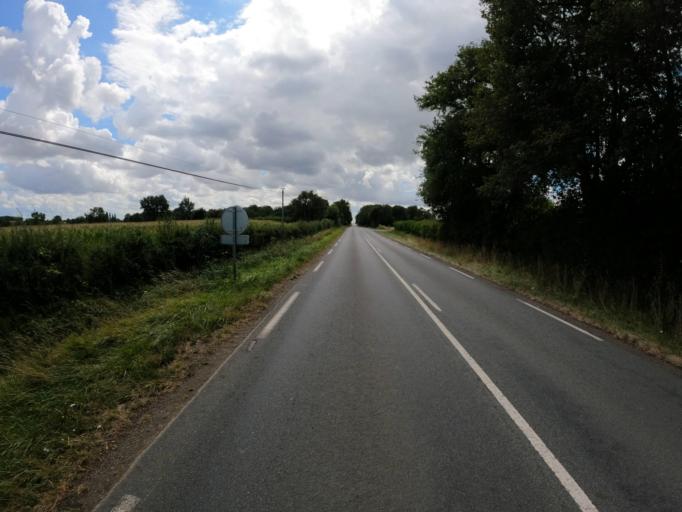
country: FR
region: Pays de la Loire
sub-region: Departement de la Sarthe
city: Juigne-sur-Sarthe
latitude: 47.8892
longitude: -0.2924
